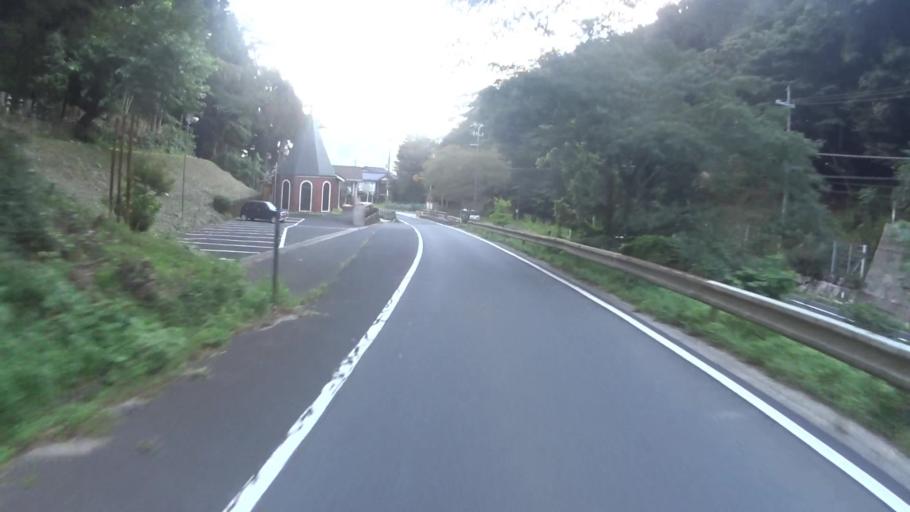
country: JP
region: Kyoto
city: Miyazu
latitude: 35.5414
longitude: 135.1105
